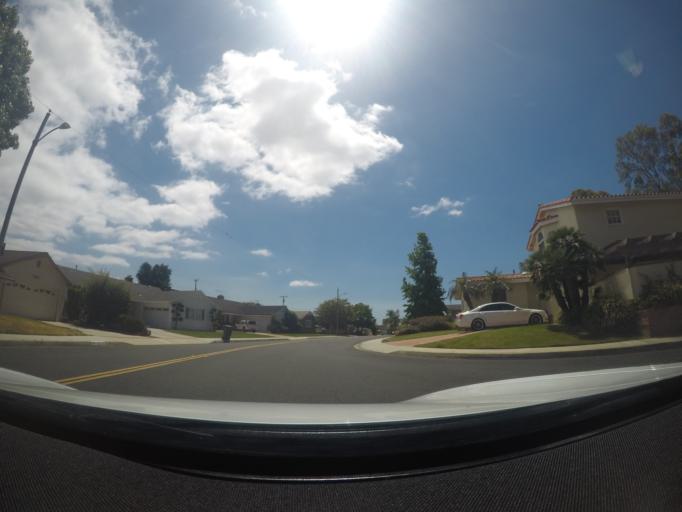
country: US
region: California
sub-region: Los Angeles County
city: Rolling Hills Estates
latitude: 33.8032
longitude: -118.3600
